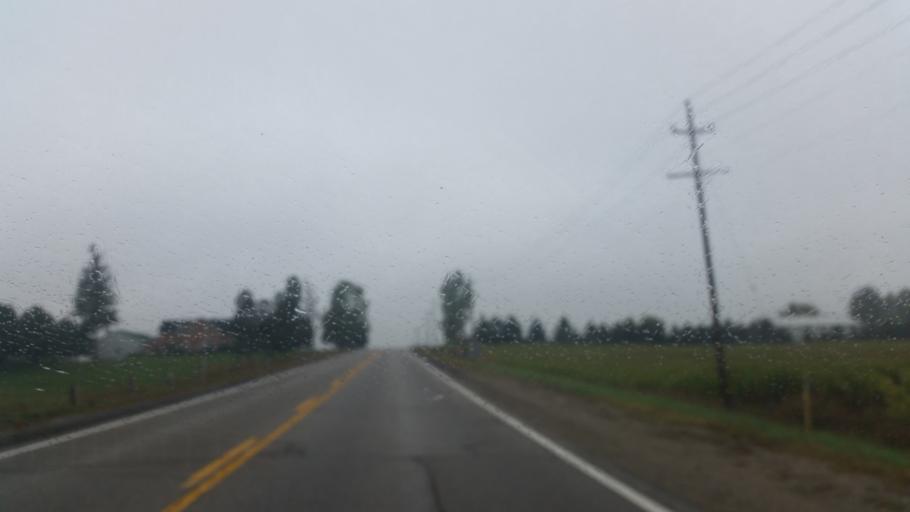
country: CA
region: Ontario
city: Waterloo
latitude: 43.6639
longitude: -80.4857
